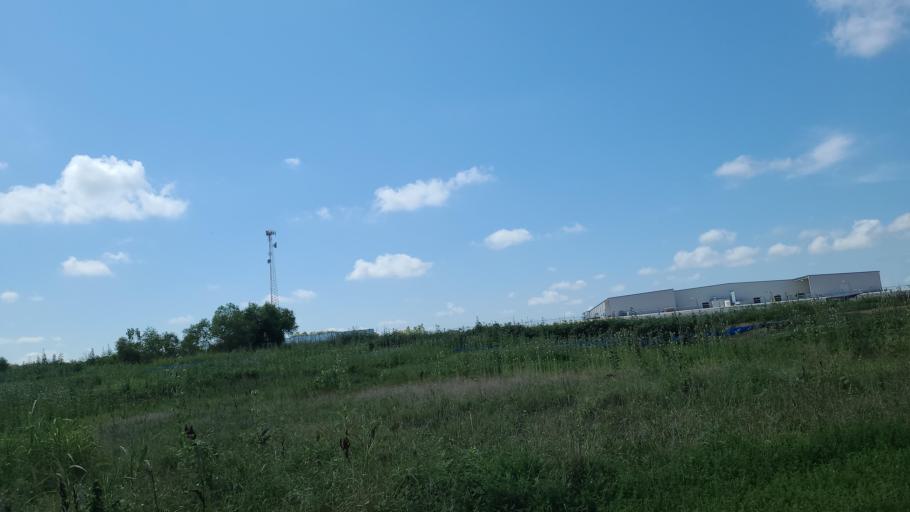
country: US
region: Kansas
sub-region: Douglas County
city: Lawrence
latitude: 38.9503
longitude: -95.1960
